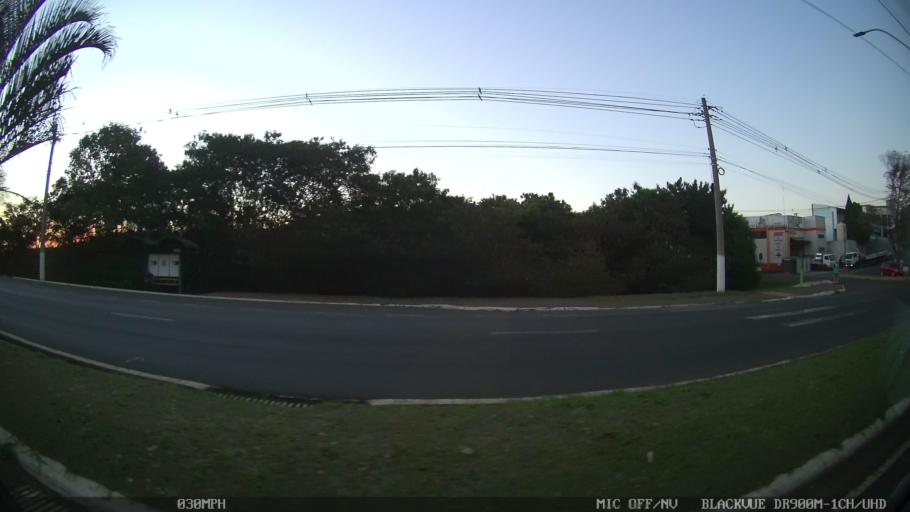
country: BR
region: Sao Paulo
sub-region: Santa Barbara D'Oeste
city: Santa Barbara d'Oeste
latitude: -22.7503
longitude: -47.3780
